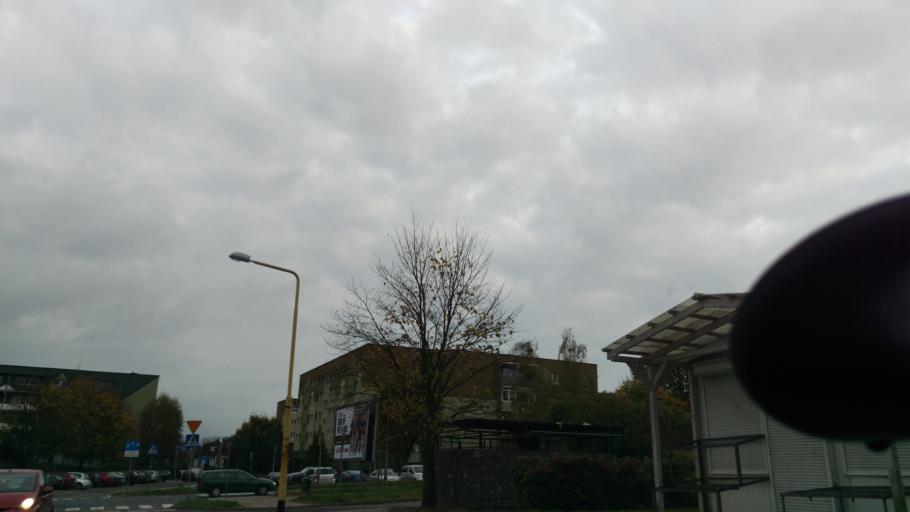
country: PL
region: West Pomeranian Voivodeship
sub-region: Szczecin
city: Szczecin
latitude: 53.3664
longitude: 14.6534
